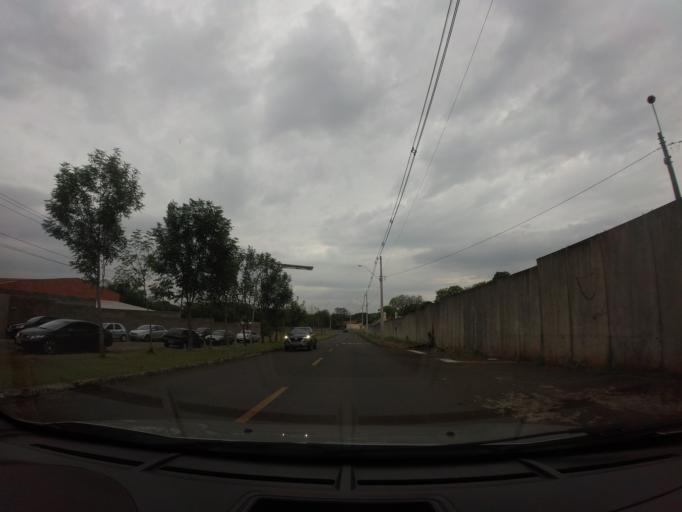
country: BR
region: Sao Paulo
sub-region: Piracicaba
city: Piracicaba
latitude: -22.7514
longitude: -47.5935
